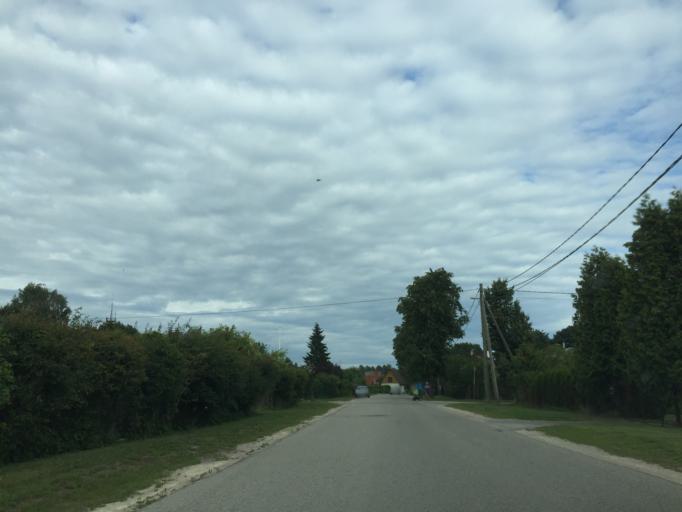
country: LV
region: Carnikava
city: Carnikava
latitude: 57.1284
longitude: 24.2666
